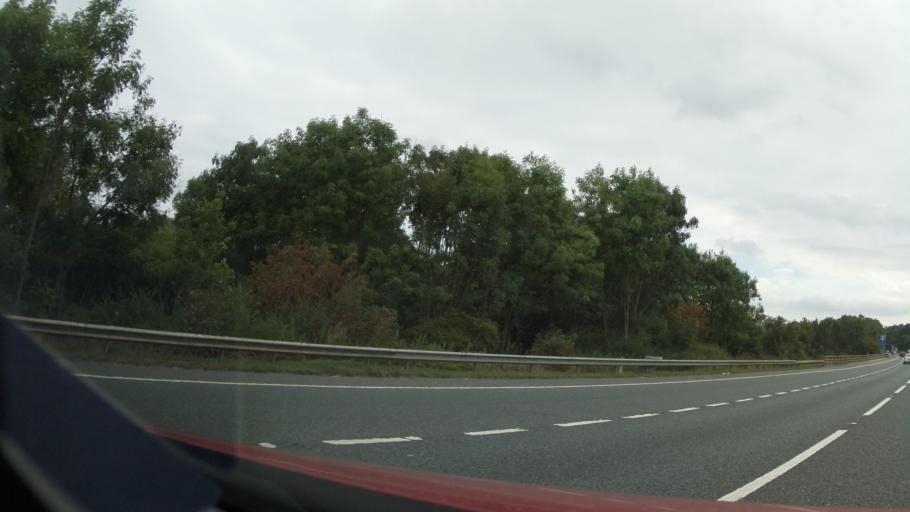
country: GB
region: England
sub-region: County Durham
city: Chester-le-Street
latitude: 54.8629
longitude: -1.5614
